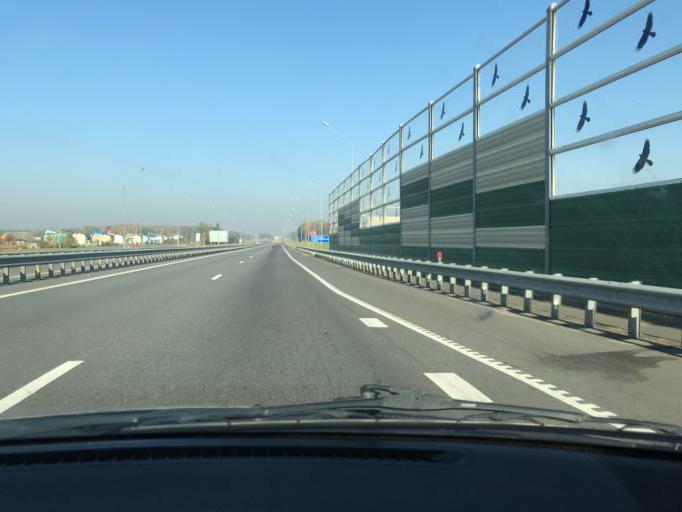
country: BY
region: Minsk
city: Slutsk
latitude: 53.2234
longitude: 27.5505
